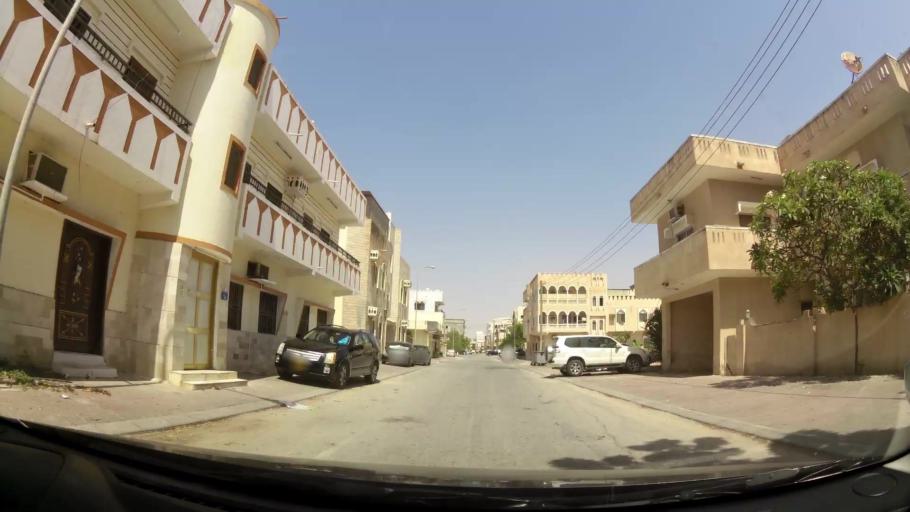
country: OM
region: Zufar
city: Salalah
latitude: 17.0210
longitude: 54.1100
